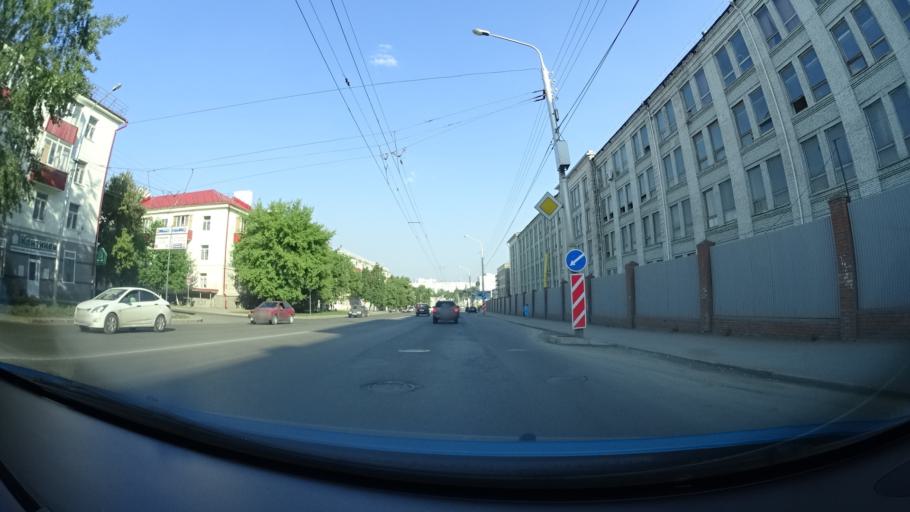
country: RU
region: Bashkortostan
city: Ufa
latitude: 54.7526
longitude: 56.0123
